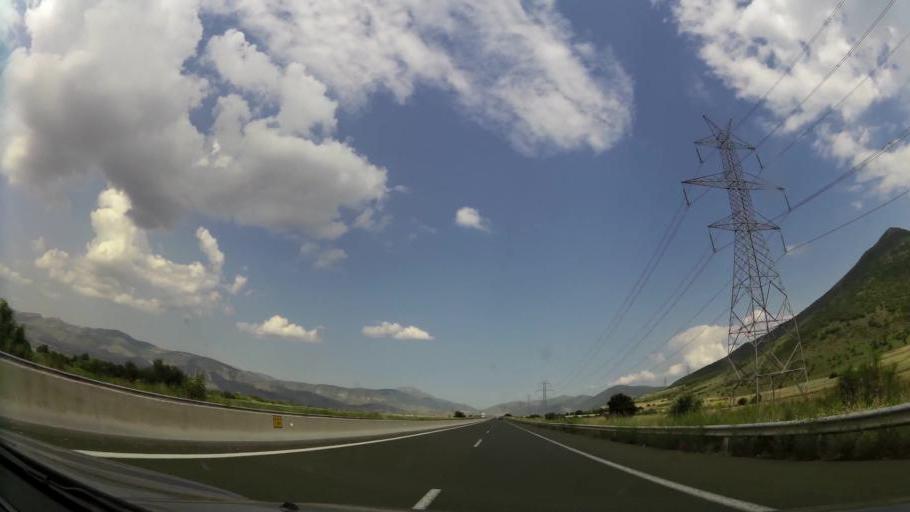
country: GR
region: West Macedonia
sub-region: Nomos Kozanis
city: Kleitos
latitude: 40.3700
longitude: 21.8817
